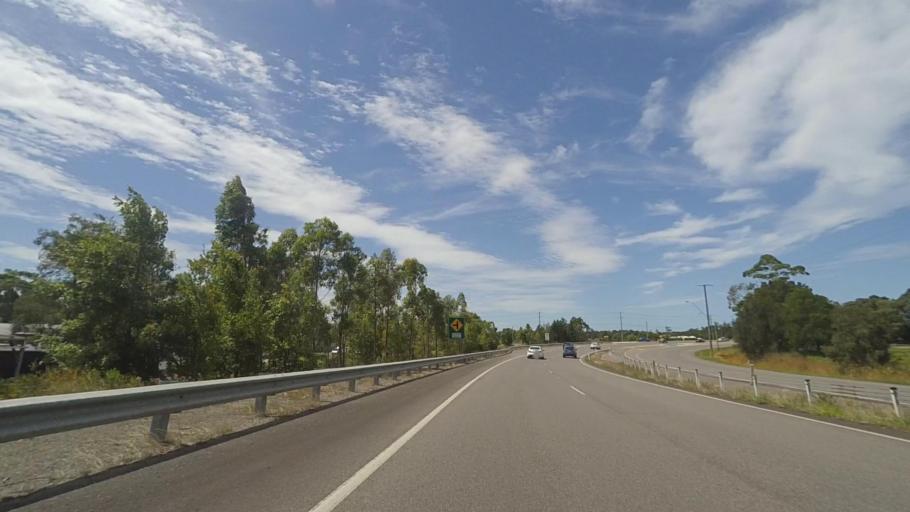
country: AU
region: New South Wales
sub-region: Port Stephens Shire
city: Anna Bay
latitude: -32.7681
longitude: 152.0122
